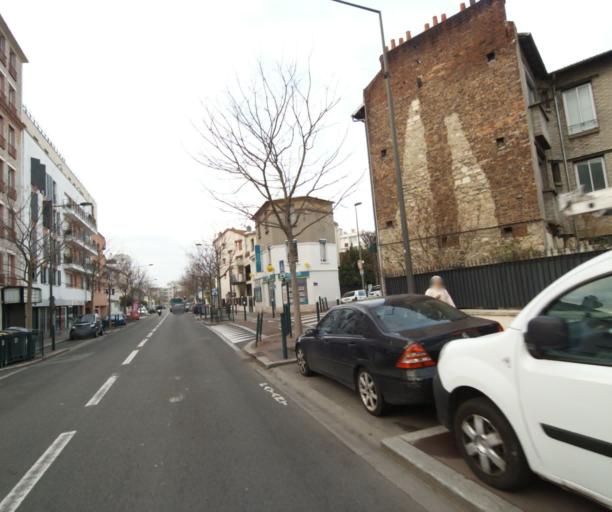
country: FR
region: Ile-de-France
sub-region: Departement des Hauts-de-Seine
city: Suresnes
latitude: 48.8654
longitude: 2.2147
